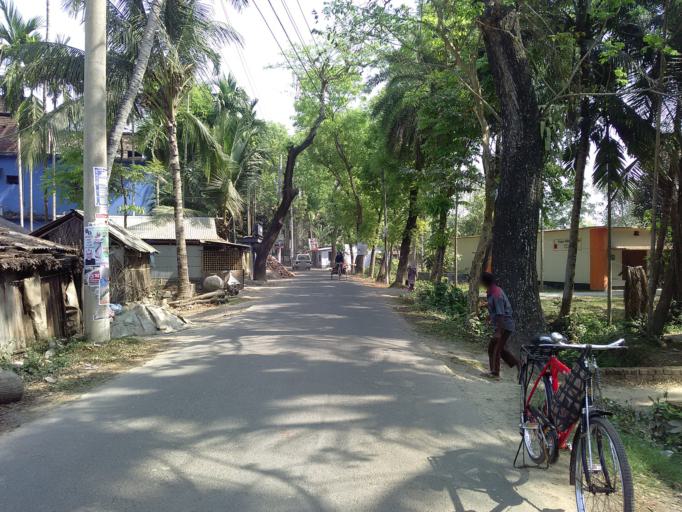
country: BD
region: Khulna
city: Khulna
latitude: 22.8880
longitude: 89.5346
